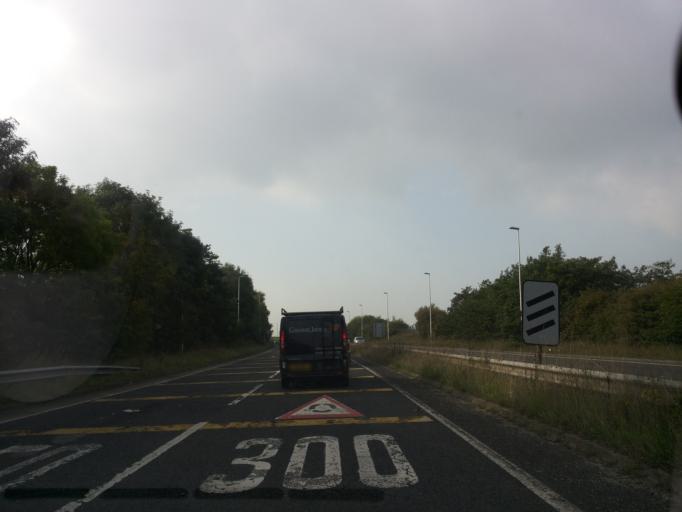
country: GB
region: England
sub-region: Lancashire
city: Great Marton
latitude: 53.7943
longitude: -2.9973
